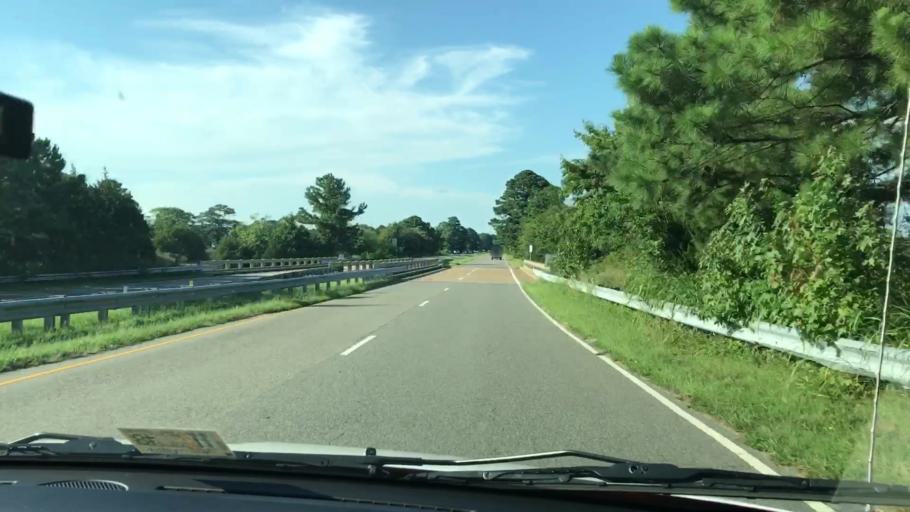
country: US
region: Virginia
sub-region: City of Hampton
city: Hampton
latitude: 37.0466
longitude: -76.3640
